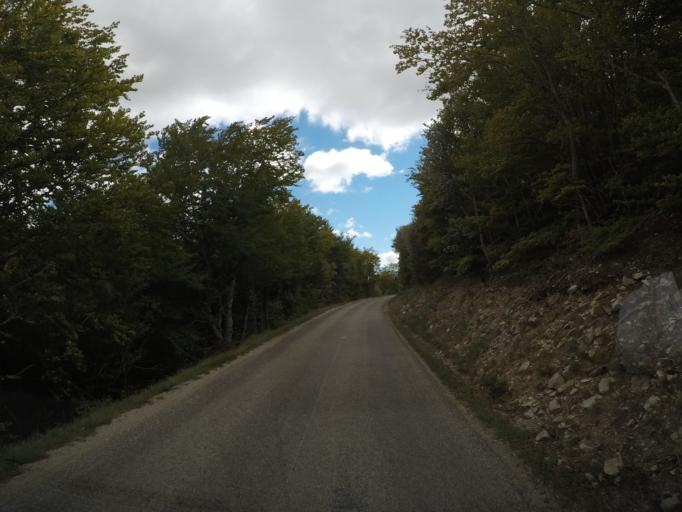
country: FR
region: Provence-Alpes-Cote d'Azur
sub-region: Departement du Vaucluse
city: Sault
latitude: 44.1609
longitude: 5.4984
